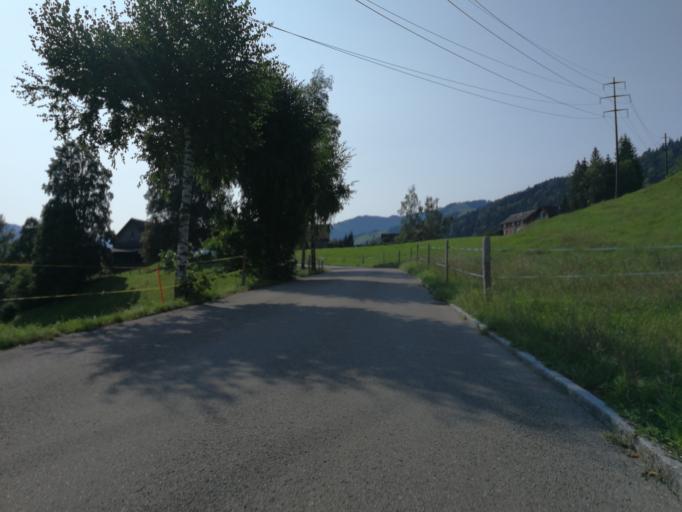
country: CH
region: Saint Gallen
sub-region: Wahlkreis Toggenburg
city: Wattwil
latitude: 47.2777
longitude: 9.0986
